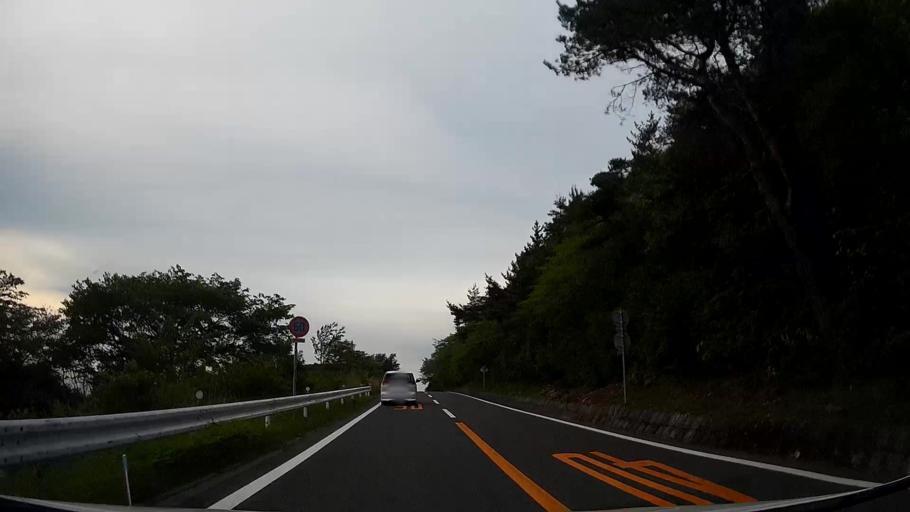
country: JP
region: Shizuoka
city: Atami
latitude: 35.0747
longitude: 139.0271
